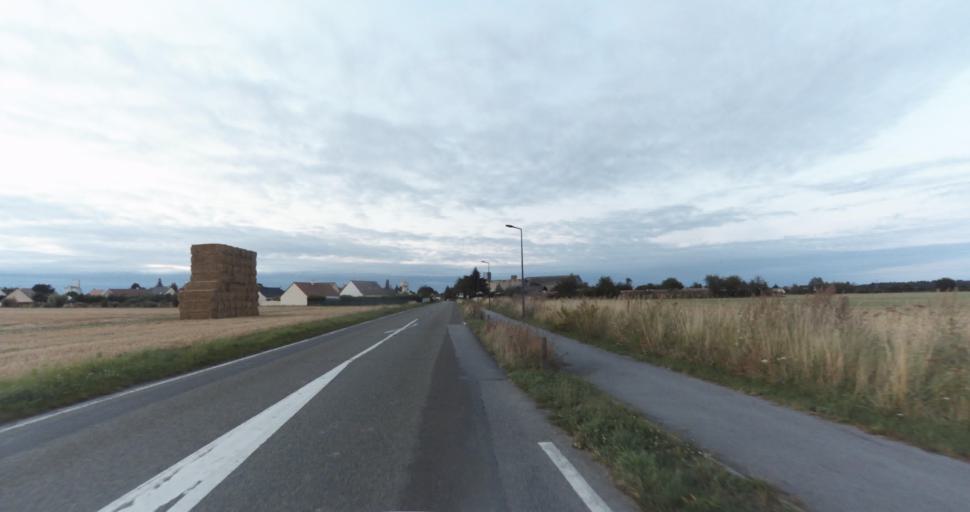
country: FR
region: Haute-Normandie
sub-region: Departement de l'Eure
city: Marcilly-sur-Eure
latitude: 48.8981
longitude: 1.2709
